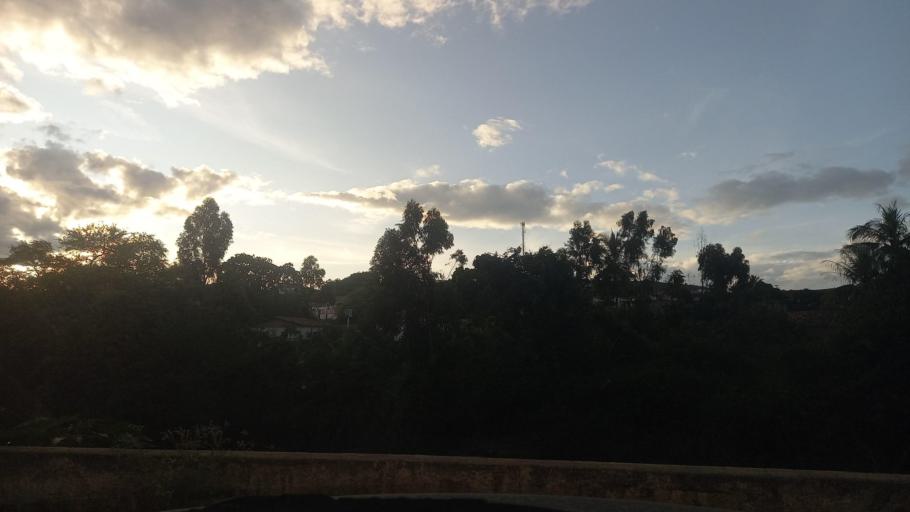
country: BR
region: Pernambuco
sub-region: Bezerros
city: Bezerros
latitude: -8.2346
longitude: -35.7539
